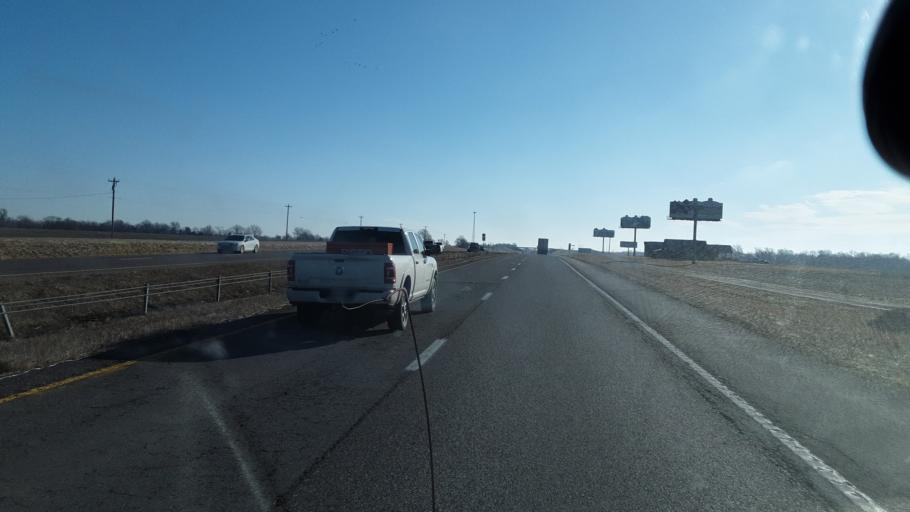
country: US
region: Missouri
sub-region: Callaway County
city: Fulton
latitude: 38.9519
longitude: -92.0239
